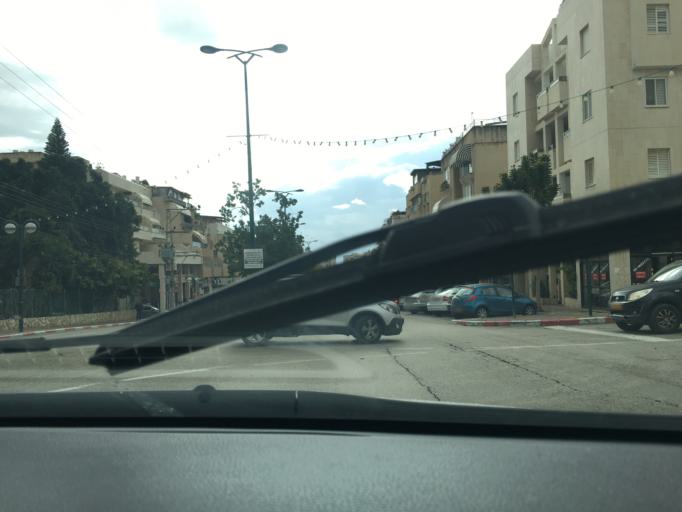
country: IL
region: Tel Aviv
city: Ramat HaSharon
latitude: 32.1426
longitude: 34.8434
